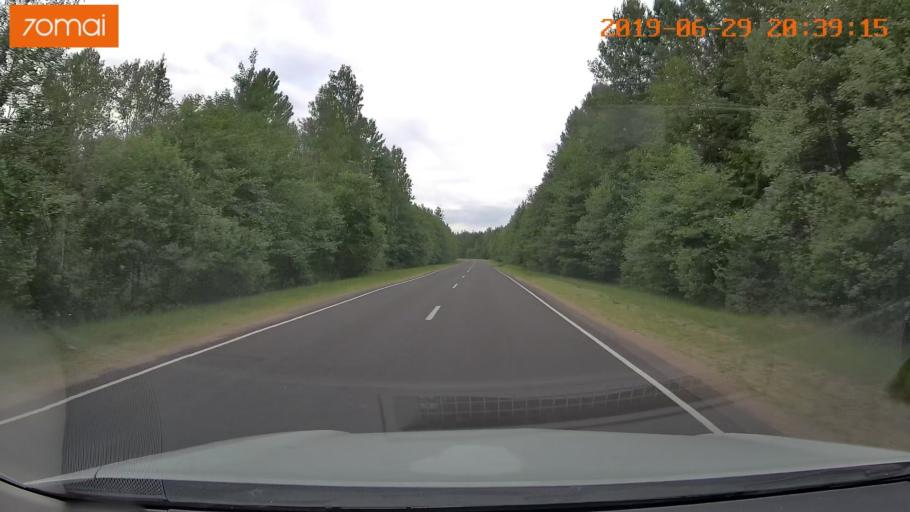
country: BY
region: Brest
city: Hantsavichy
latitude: 52.5600
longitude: 26.3631
